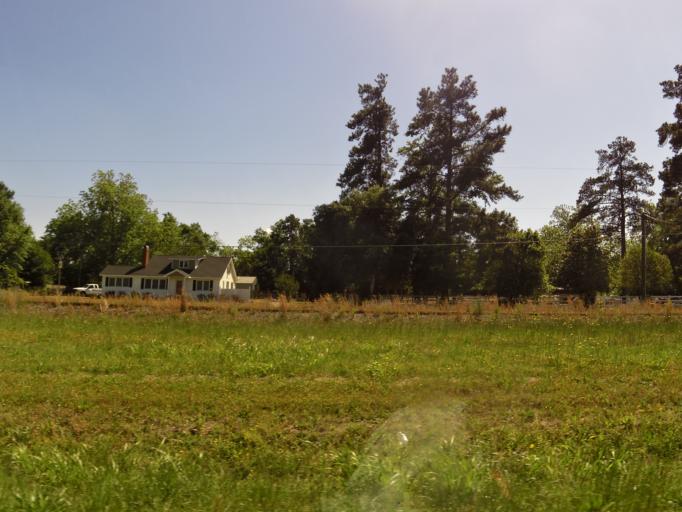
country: US
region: South Carolina
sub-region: Aiken County
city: Aiken
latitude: 33.5297
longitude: -81.6388
